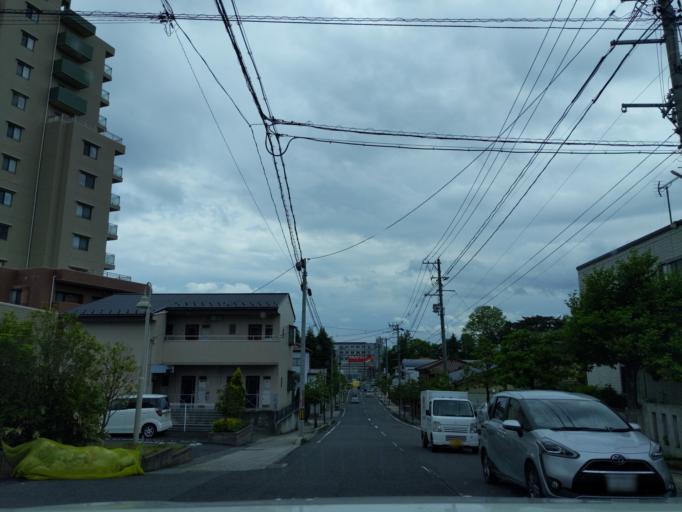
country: JP
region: Fukushima
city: Koriyama
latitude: 37.3930
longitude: 140.3720
